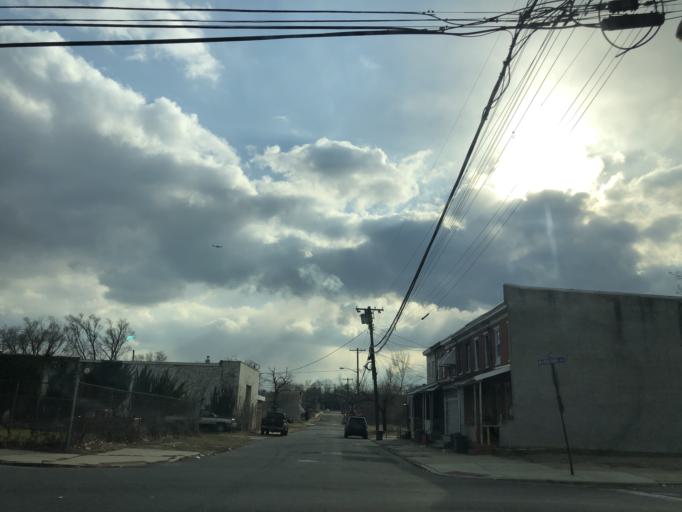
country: US
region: New Jersey
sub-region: Camden County
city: Camden
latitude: 39.9156
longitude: -75.1141
